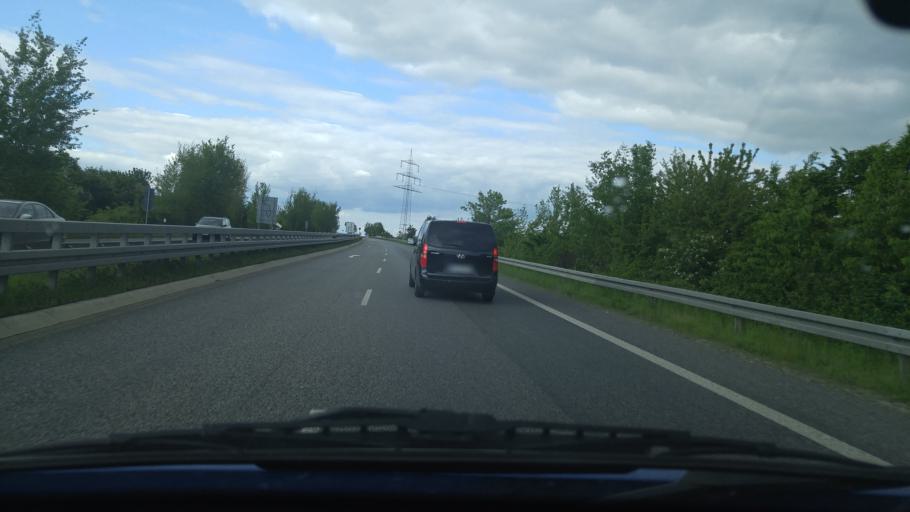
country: DE
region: Hesse
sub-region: Regierungsbezirk Darmstadt
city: Bad Vilbel
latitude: 50.1966
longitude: 8.7335
